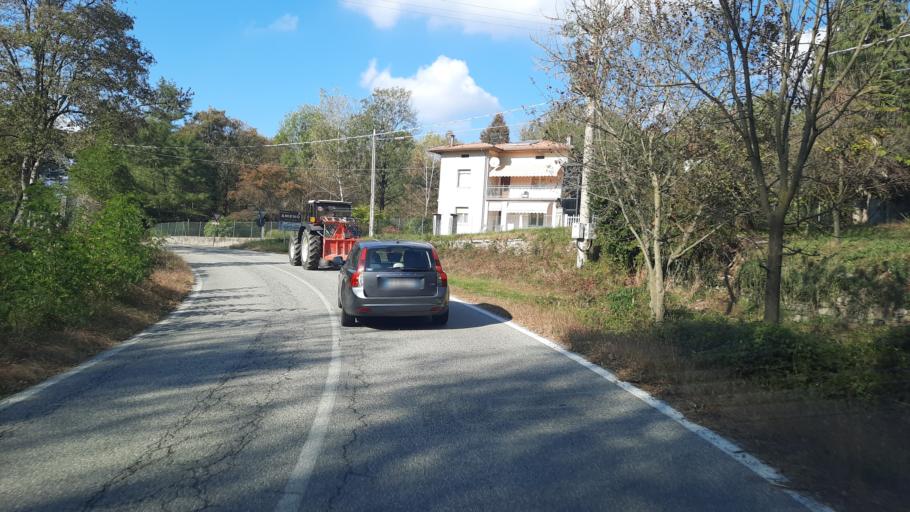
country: IT
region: Piedmont
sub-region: Provincia di Novara
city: Ameno
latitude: 45.7771
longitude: 8.4378
